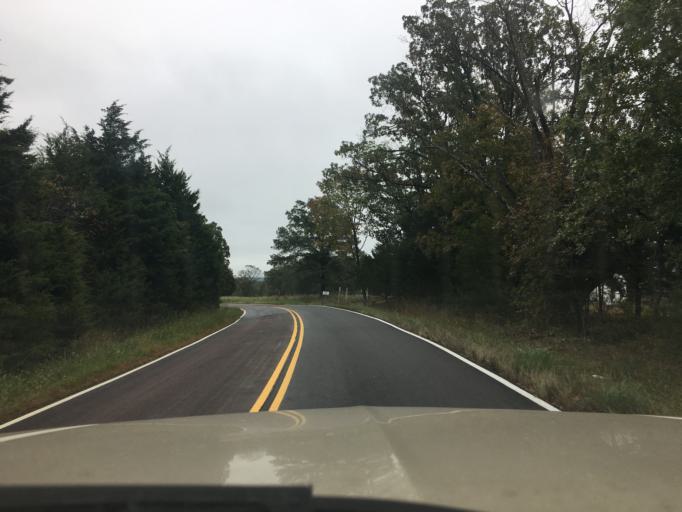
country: US
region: Missouri
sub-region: Crawford County
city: Cuba
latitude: 38.1908
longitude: -91.4717
